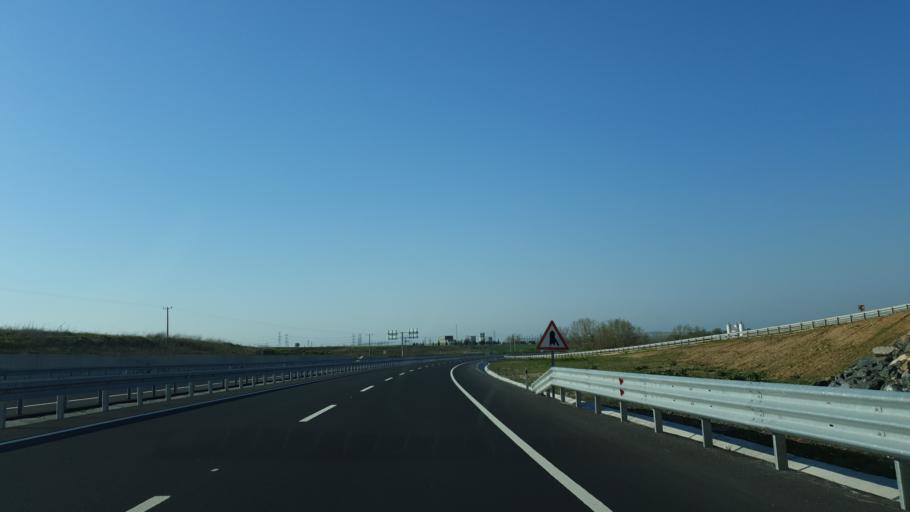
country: TR
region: Tekirdag
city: Corlu
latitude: 41.1276
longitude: 27.7548
